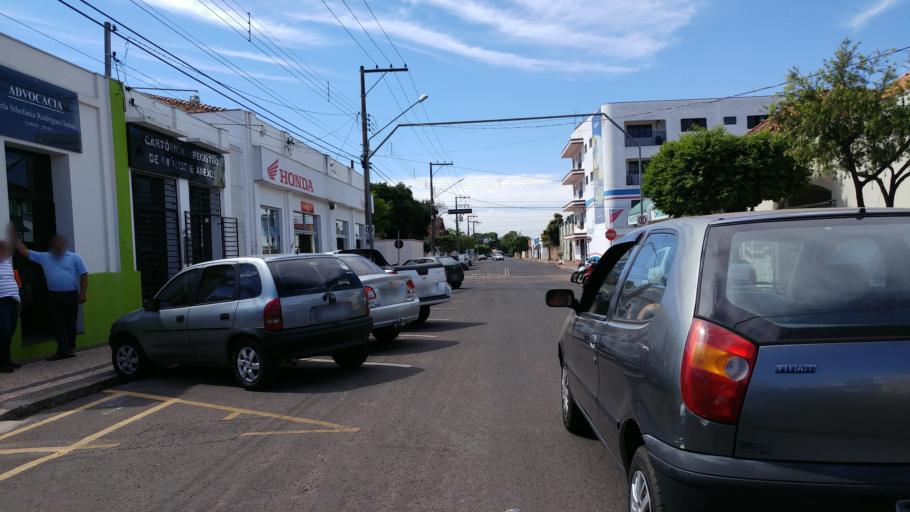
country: BR
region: Sao Paulo
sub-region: Paraguacu Paulista
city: Paraguacu Paulista
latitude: -22.4127
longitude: -50.5749
